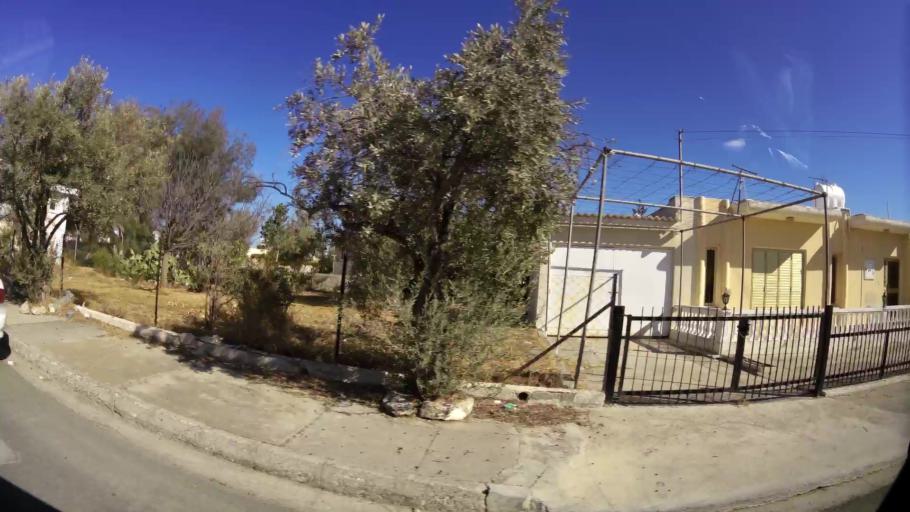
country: CY
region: Larnaka
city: Larnaca
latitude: 34.9377
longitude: 33.6162
